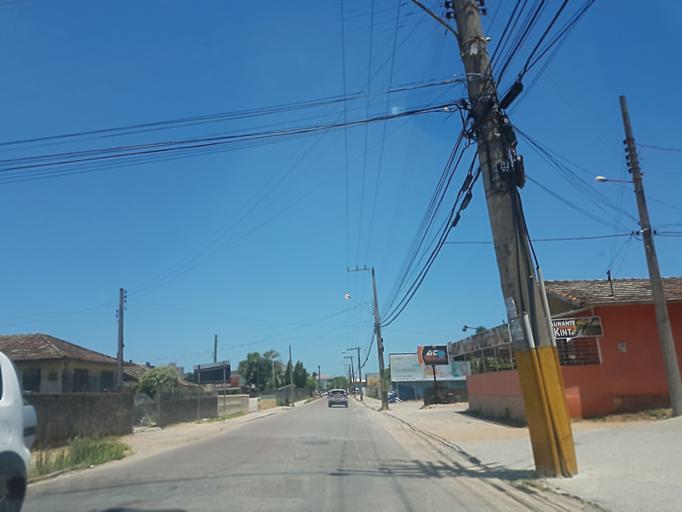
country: BR
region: Santa Catarina
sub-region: Tubarao
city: Tubarao
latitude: -28.4734
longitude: -49.0323
